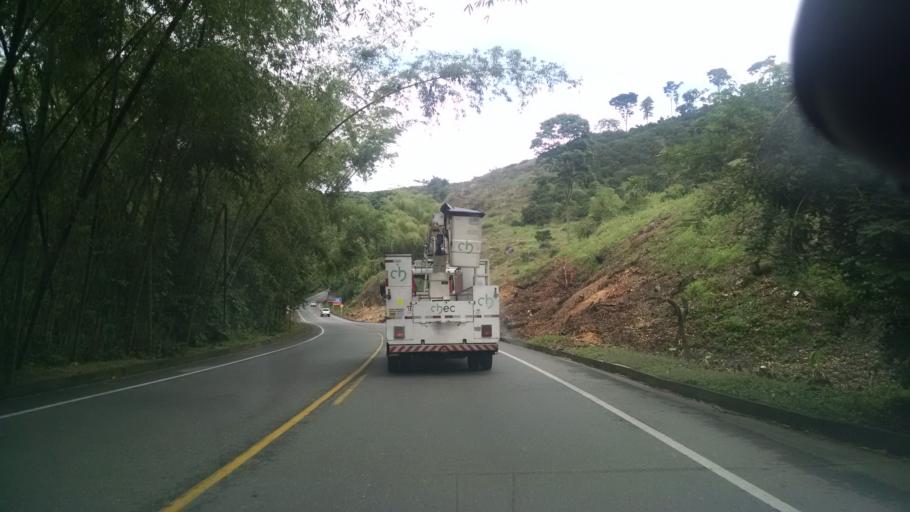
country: CO
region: Caldas
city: Palestina
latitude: 5.0618
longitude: -75.6112
